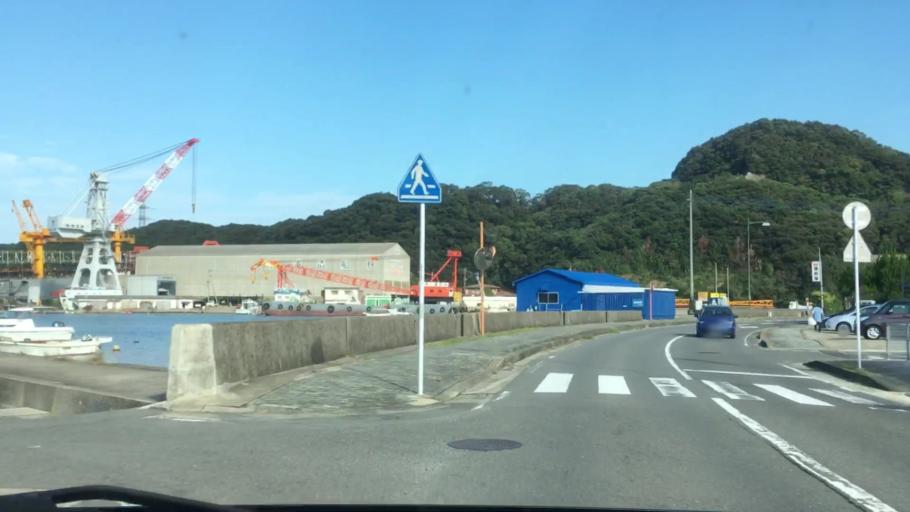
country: JP
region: Nagasaki
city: Sasebo
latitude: 32.9456
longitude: 129.6380
